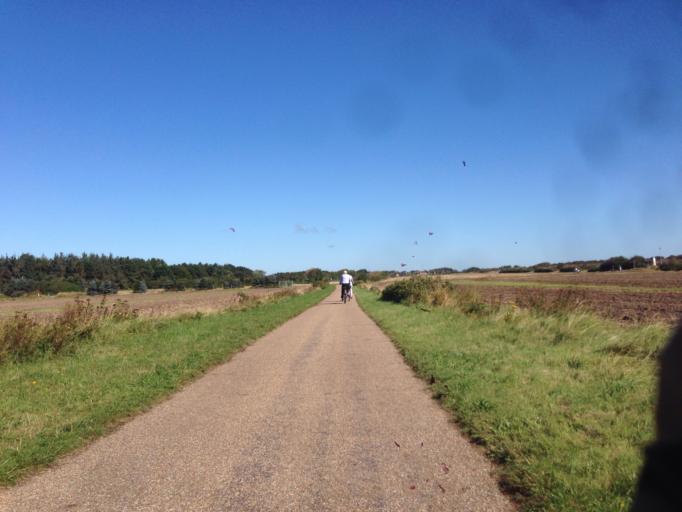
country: DE
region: Schleswig-Holstein
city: Tinnum
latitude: 54.9412
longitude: 8.3318
